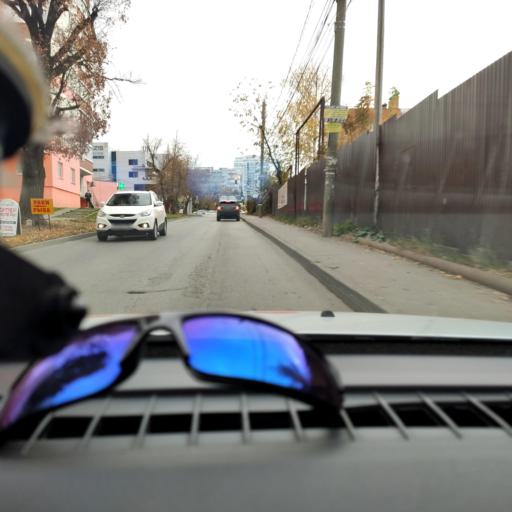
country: RU
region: Samara
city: Samara
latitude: 53.2540
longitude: 50.2006
